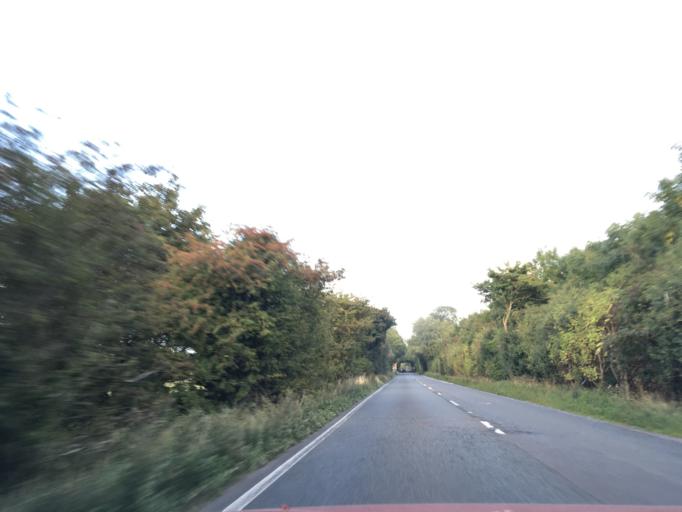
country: GB
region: England
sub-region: Gloucestershire
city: Northleach
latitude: 51.8503
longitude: -1.8171
